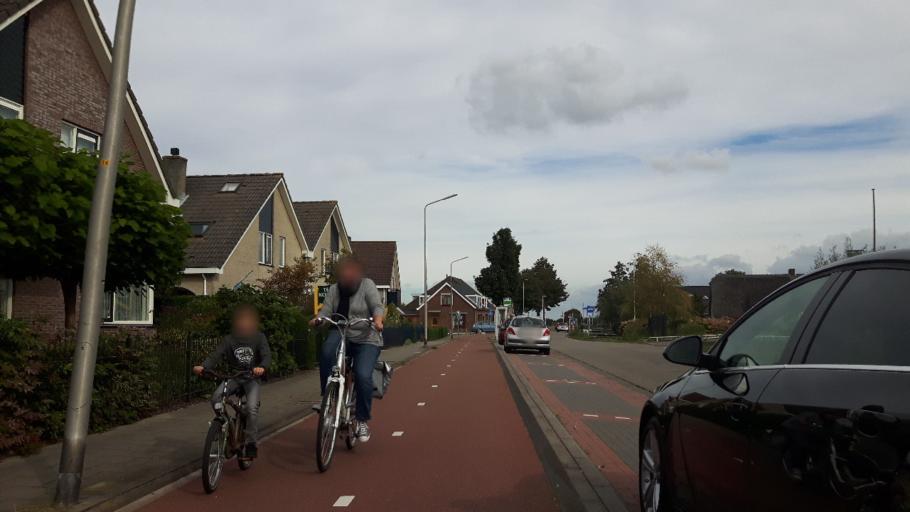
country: NL
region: South Holland
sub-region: Gemeente Nieuwkoop
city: Nieuwkoop
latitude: 52.1540
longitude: 4.7861
